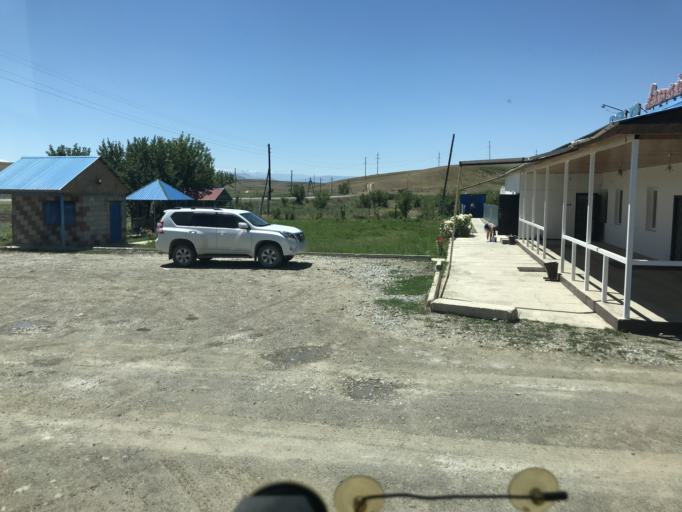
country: KZ
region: Almaty Oblysy
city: Sarkand
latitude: 45.6396
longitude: 80.2254
